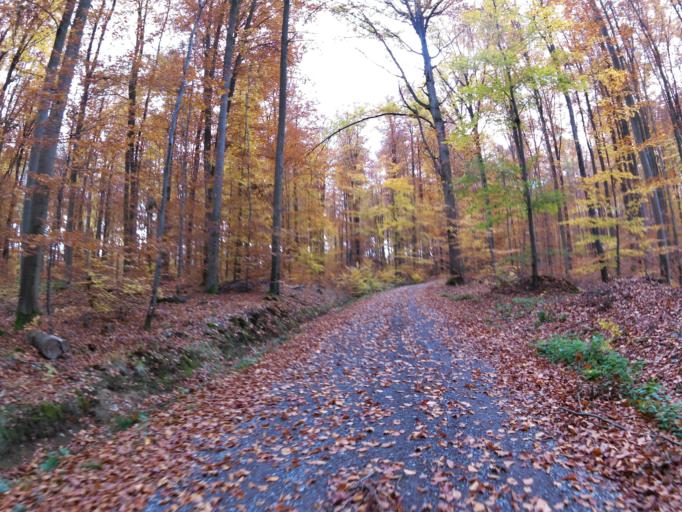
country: DE
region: Bavaria
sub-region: Regierungsbezirk Unterfranken
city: Kist
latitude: 49.7250
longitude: 9.8172
